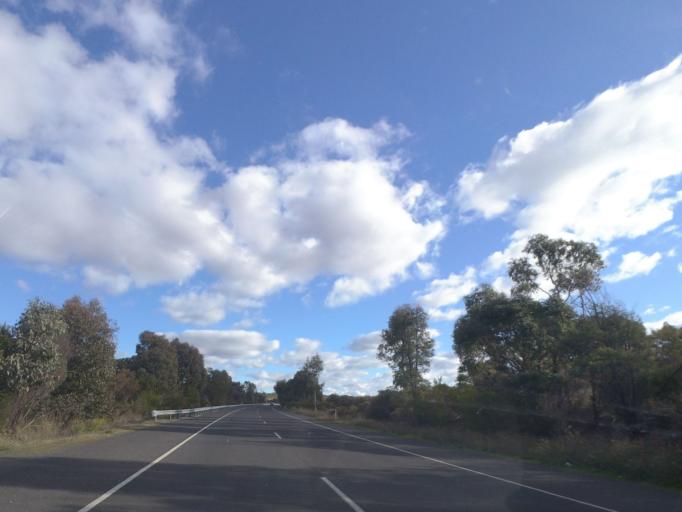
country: AU
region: Victoria
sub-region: Mount Alexander
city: Castlemaine
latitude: -37.1003
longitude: 144.3222
